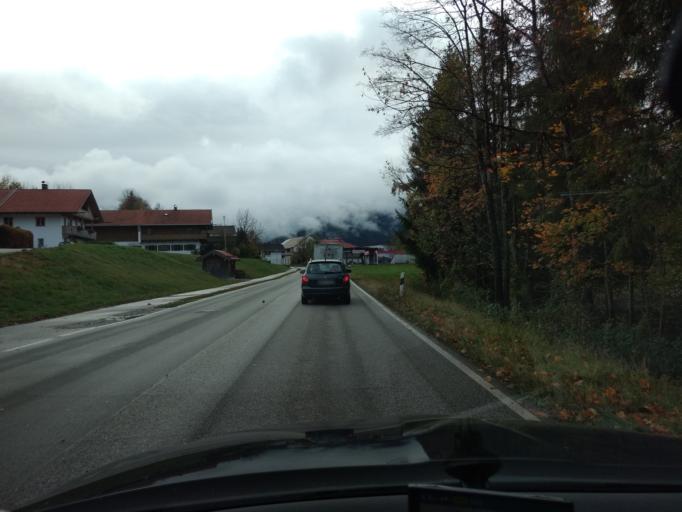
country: DE
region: Bavaria
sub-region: Upper Bavaria
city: Lenggries
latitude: 47.6542
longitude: 11.5890
